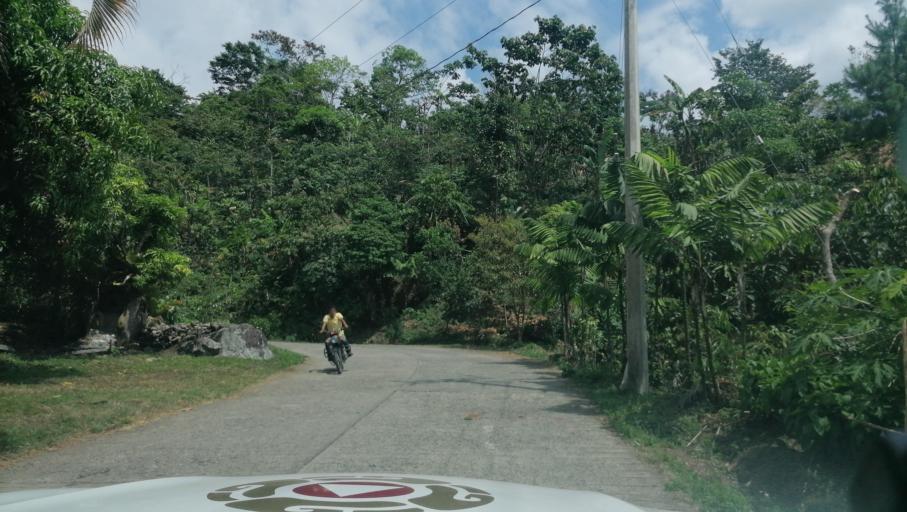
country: MX
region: Chiapas
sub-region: Cacahoatan
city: Benito Juarez
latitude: 15.1129
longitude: -92.2094
